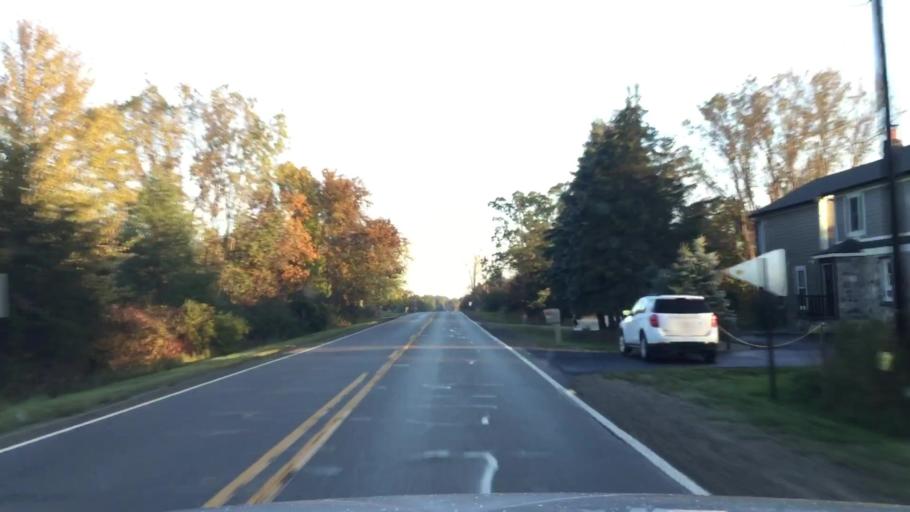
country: US
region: Michigan
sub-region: Livingston County
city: Howell
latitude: 42.6899
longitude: -83.9371
